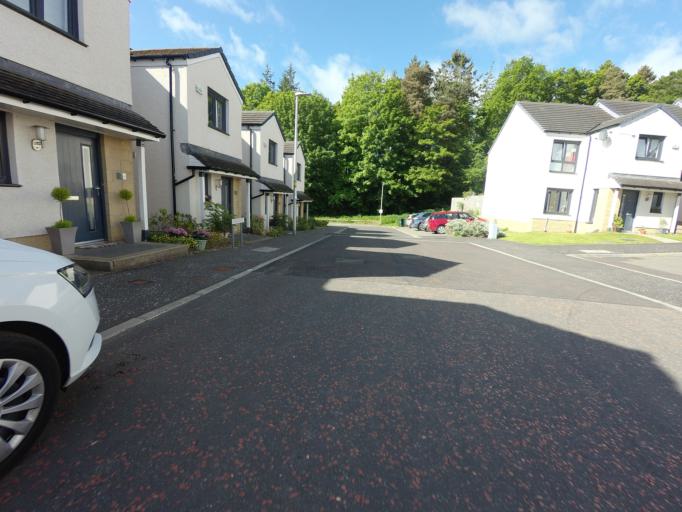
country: GB
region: Scotland
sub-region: Perth and Kinross
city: Auchterarder
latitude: 56.2920
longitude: -3.7142
